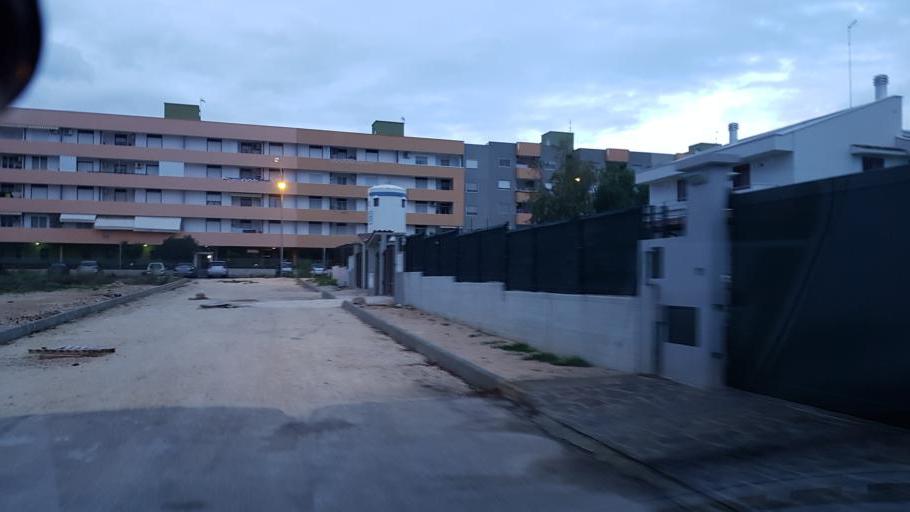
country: IT
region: Apulia
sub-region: Provincia di Taranto
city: Paolo VI
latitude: 40.5307
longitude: 17.2848
